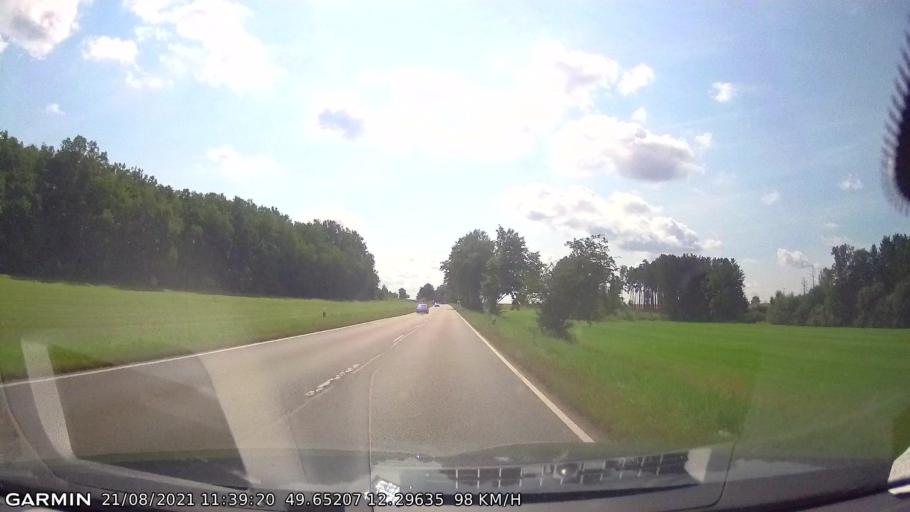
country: DE
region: Bavaria
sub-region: Upper Palatinate
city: Waldthurn
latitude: 49.6521
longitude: 12.2963
